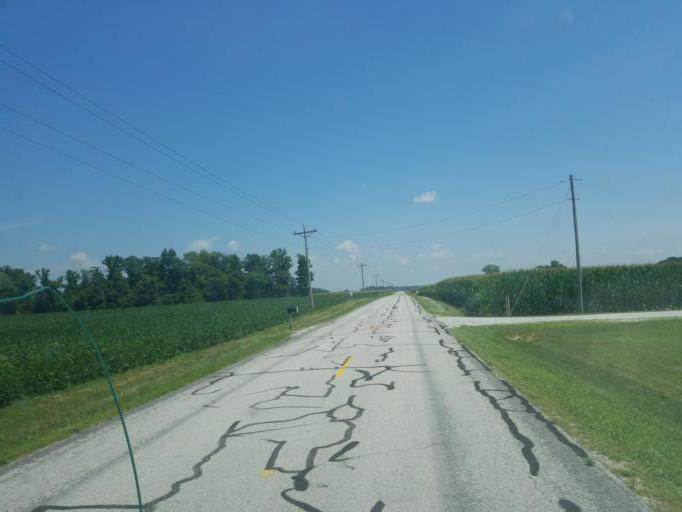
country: US
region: Ohio
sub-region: Auglaize County
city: Wapakoneta
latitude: 40.5404
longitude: -84.2723
